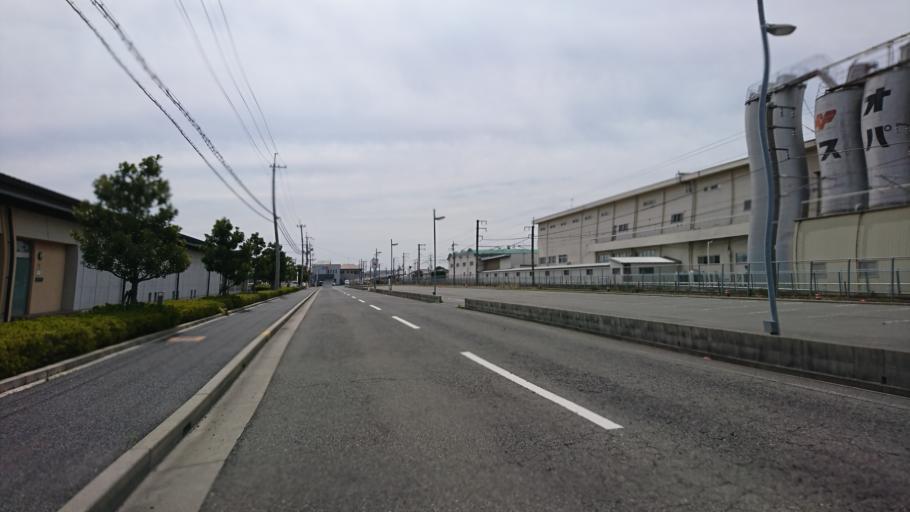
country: JP
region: Hyogo
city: Kakogawacho-honmachi
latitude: 34.7377
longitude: 134.8768
